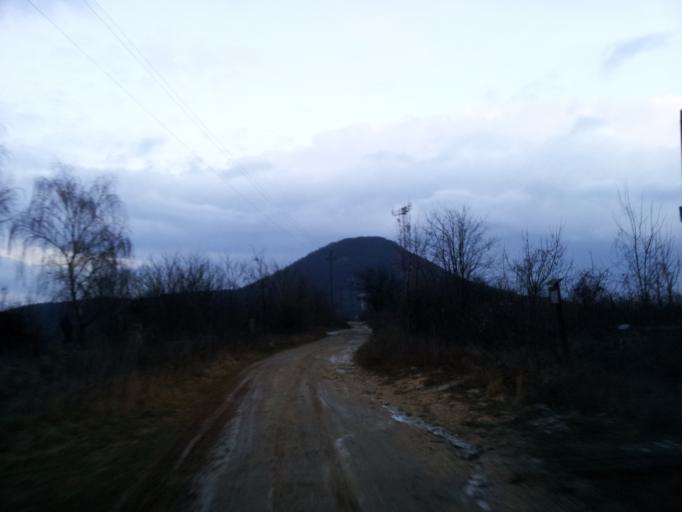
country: HU
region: Pest
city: Csobanka
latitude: 47.6387
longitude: 18.9581
